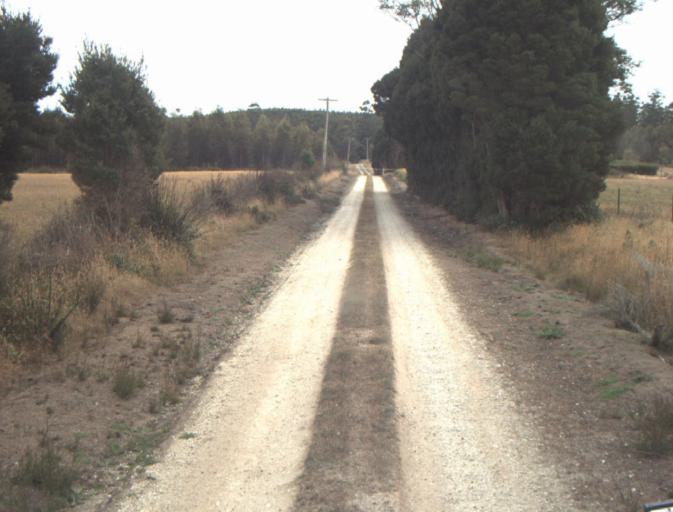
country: AU
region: Tasmania
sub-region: Launceston
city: Mayfield
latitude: -41.1903
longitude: 147.1674
